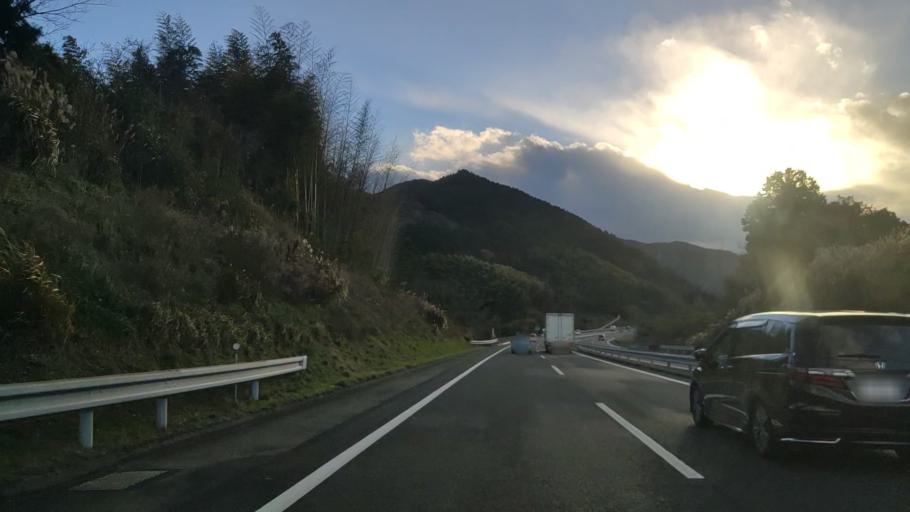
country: JP
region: Ehime
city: Saijo
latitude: 33.8675
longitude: 133.0583
